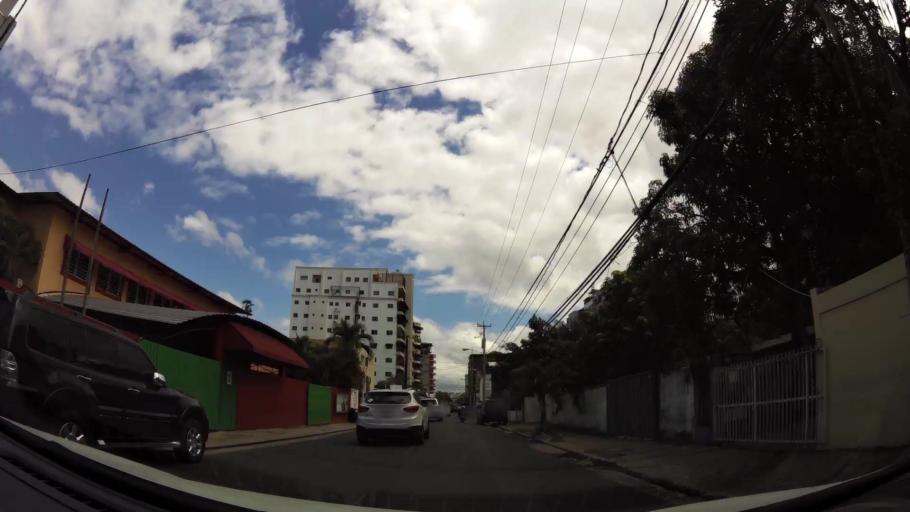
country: DO
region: Nacional
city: Bella Vista
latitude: 18.4599
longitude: -69.9479
